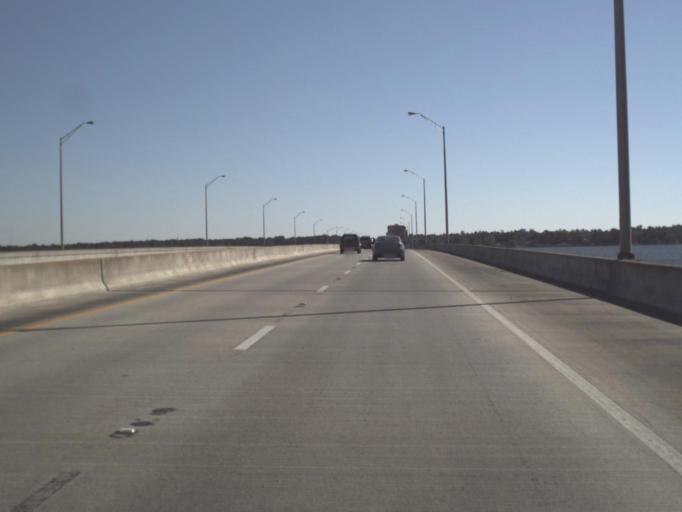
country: US
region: Florida
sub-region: Seminole County
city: Oviedo
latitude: 28.7126
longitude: -81.2396
